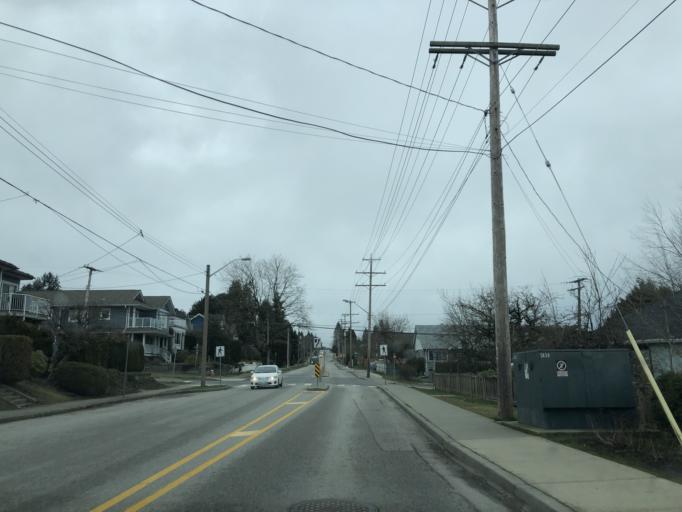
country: CA
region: British Columbia
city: New Westminster
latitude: 49.2231
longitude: -122.8987
